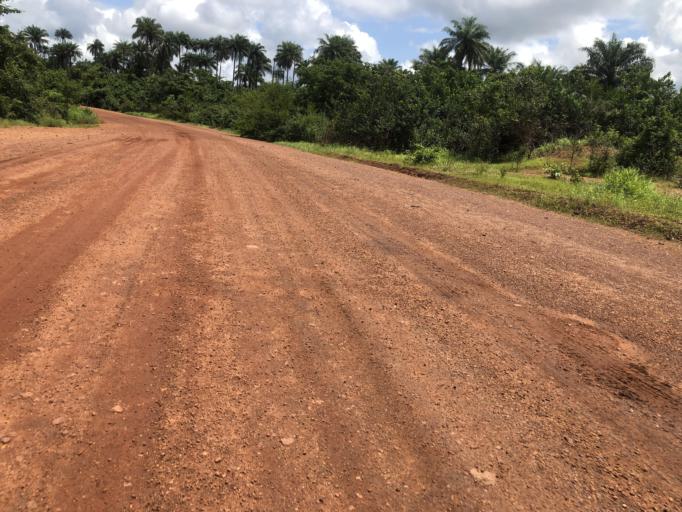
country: SL
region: Northern Province
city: Port Loko
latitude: 8.7146
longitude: -12.8324
